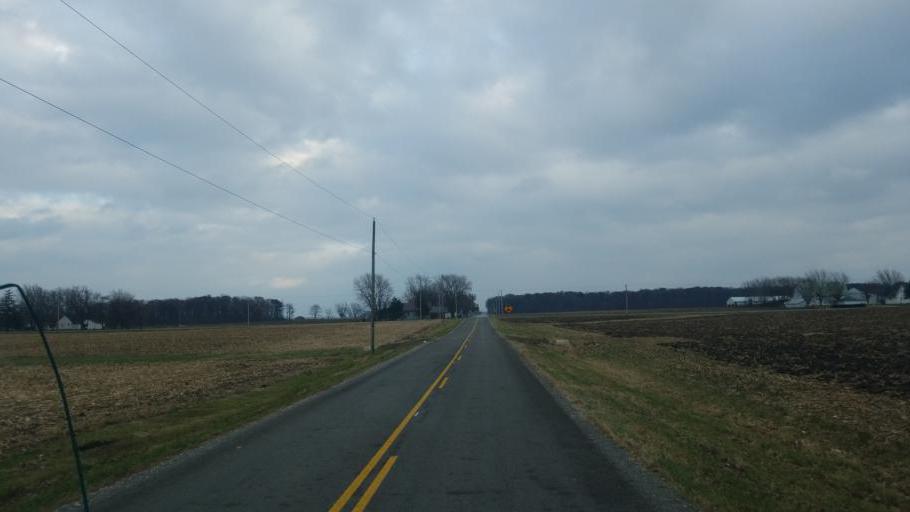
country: US
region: Ohio
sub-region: Mercer County
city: Coldwater
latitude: 40.5089
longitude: -84.6506
